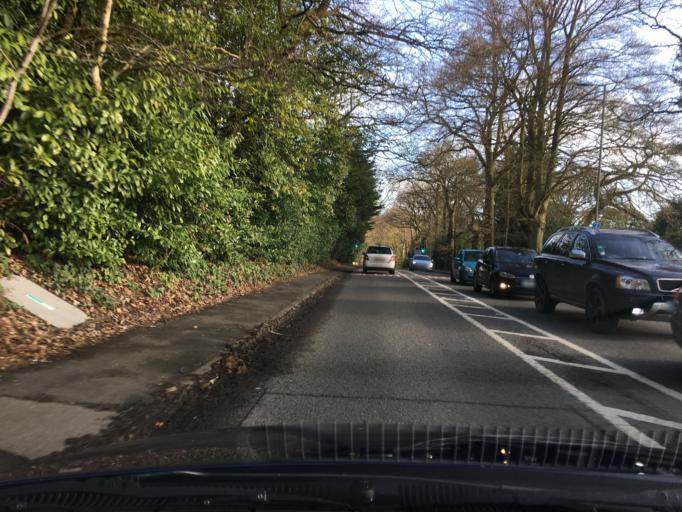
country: GB
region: England
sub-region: Bracknell Forest
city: Sandhurst
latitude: 51.3523
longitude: -0.7992
